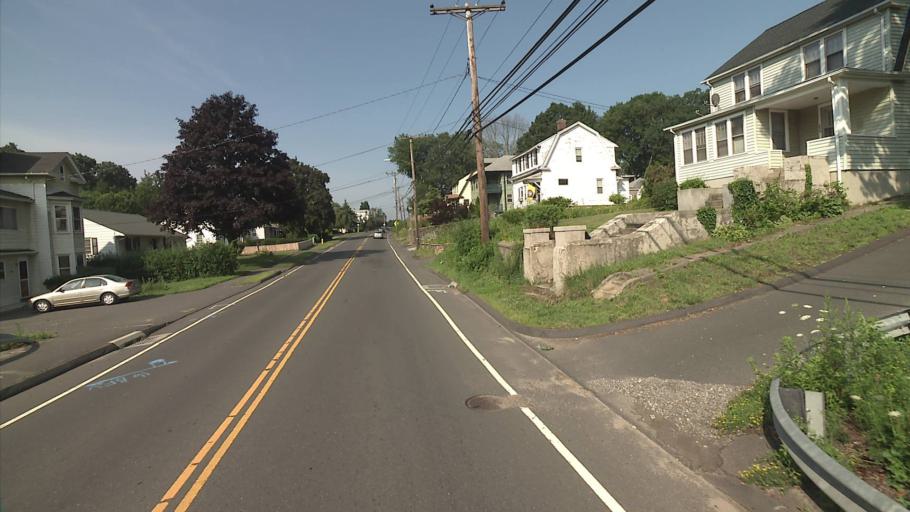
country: US
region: Connecticut
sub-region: New Haven County
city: Prospect
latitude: 41.5446
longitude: -72.9885
